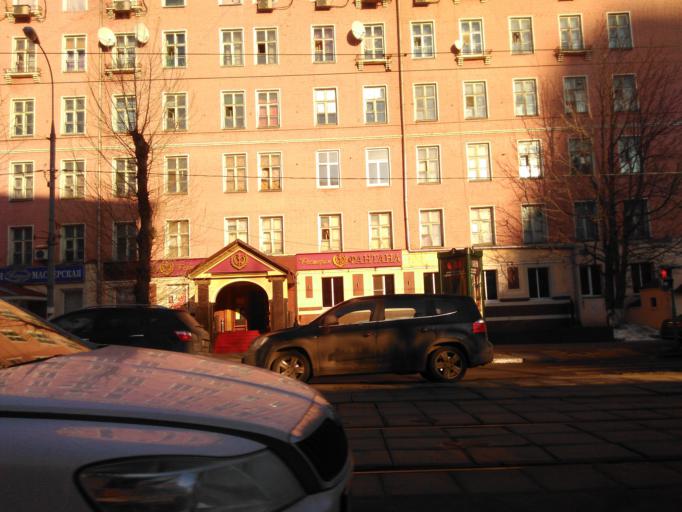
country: RU
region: Moskovskaya
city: Cheremushki
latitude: 55.6795
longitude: 37.5717
